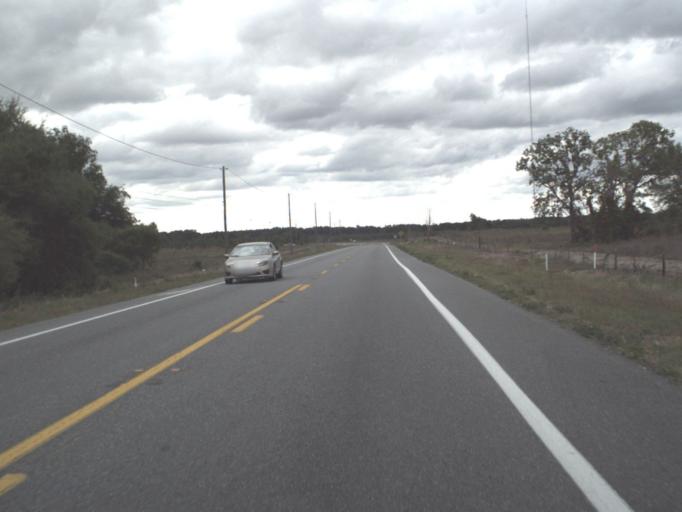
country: US
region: Florida
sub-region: Marion County
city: Ocala
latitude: 29.2553
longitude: -82.0697
